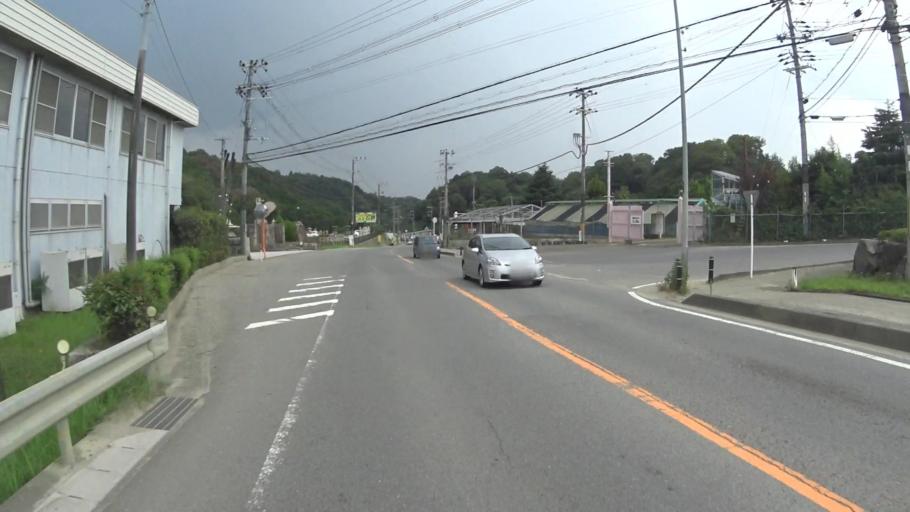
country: JP
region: Kyoto
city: Uji
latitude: 34.8368
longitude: 135.8278
